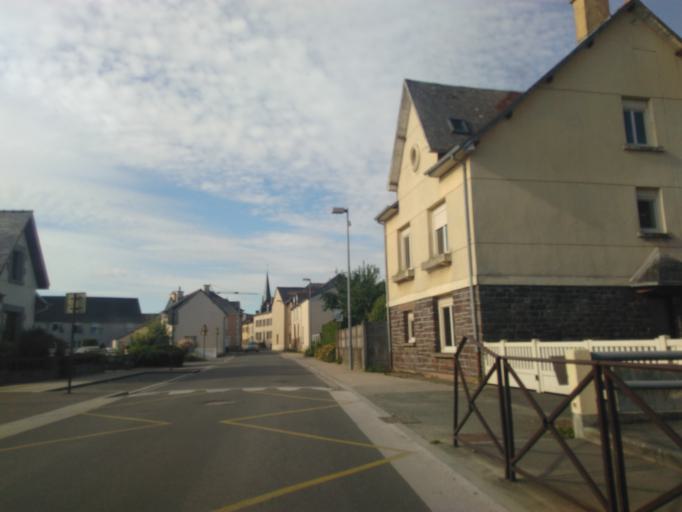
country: FR
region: Brittany
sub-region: Departement d'Ille-et-Vilaine
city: Romille
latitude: 48.2136
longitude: -1.8928
